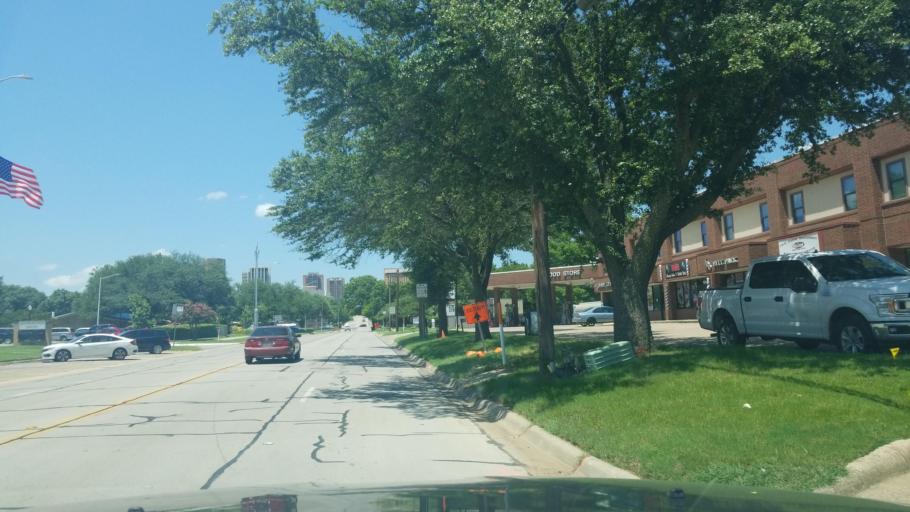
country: US
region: Texas
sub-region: Denton County
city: Denton
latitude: 33.2187
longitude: -97.1273
